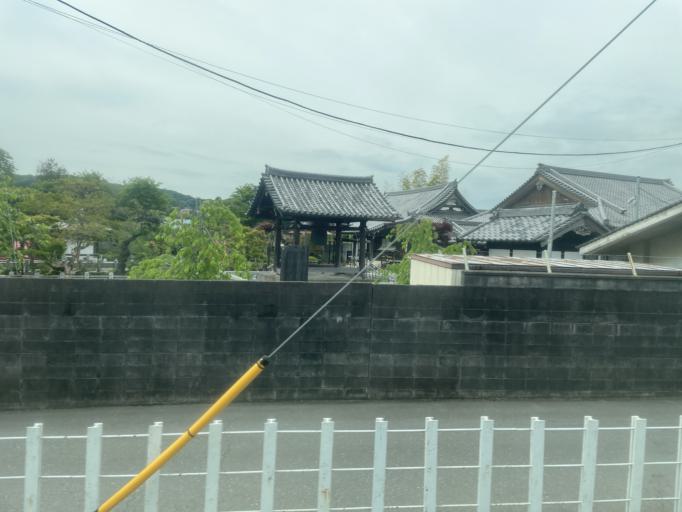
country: JP
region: Saitama
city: Hanno
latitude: 35.8399
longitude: 139.3469
